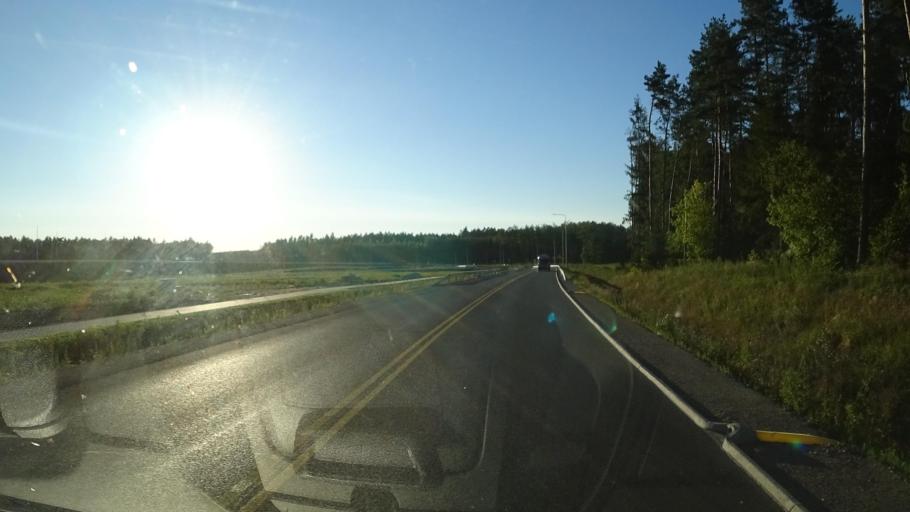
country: PL
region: Warmian-Masurian Voivodeship
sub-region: Powiat elcki
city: Elk
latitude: 53.8385
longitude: 22.4211
